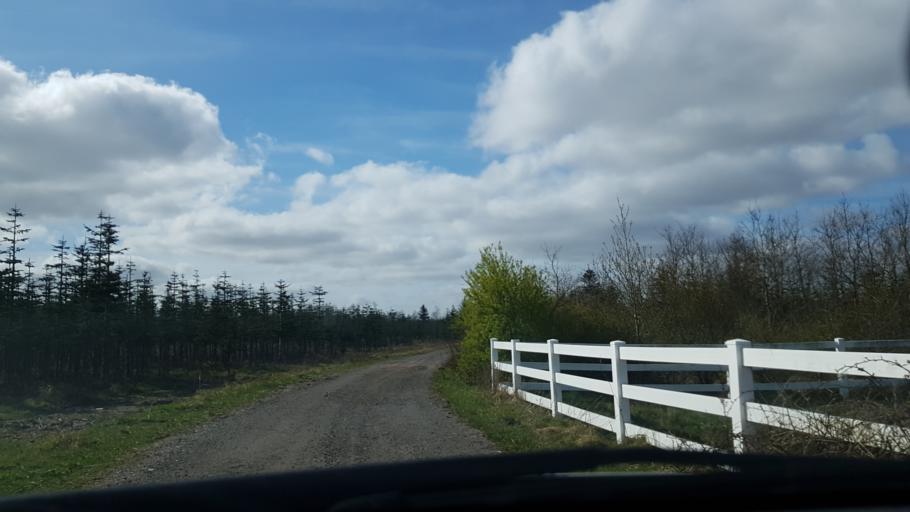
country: DK
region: South Denmark
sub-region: Haderslev Kommune
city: Gram
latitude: 55.2991
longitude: 8.9805
